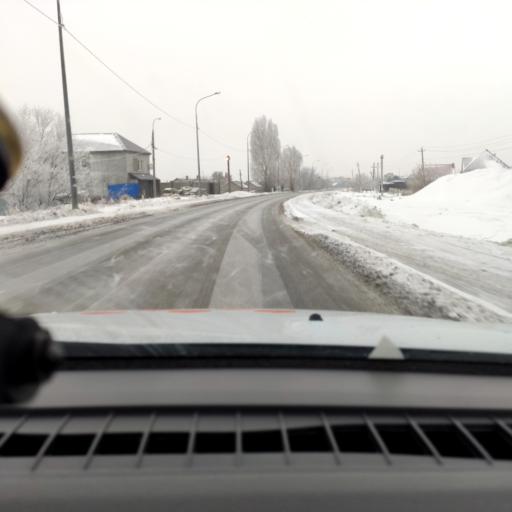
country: RU
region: Samara
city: Dubovyy Umet
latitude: 53.0770
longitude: 50.2077
